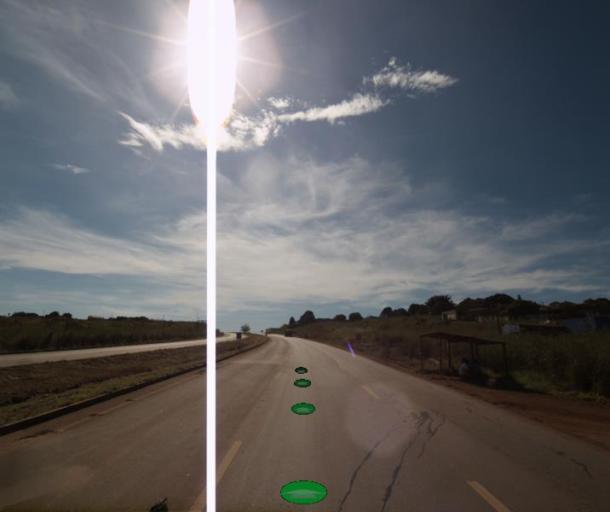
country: BR
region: Federal District
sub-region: Brasilia
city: Brasilia
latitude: -15.7560
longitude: -48.3324
